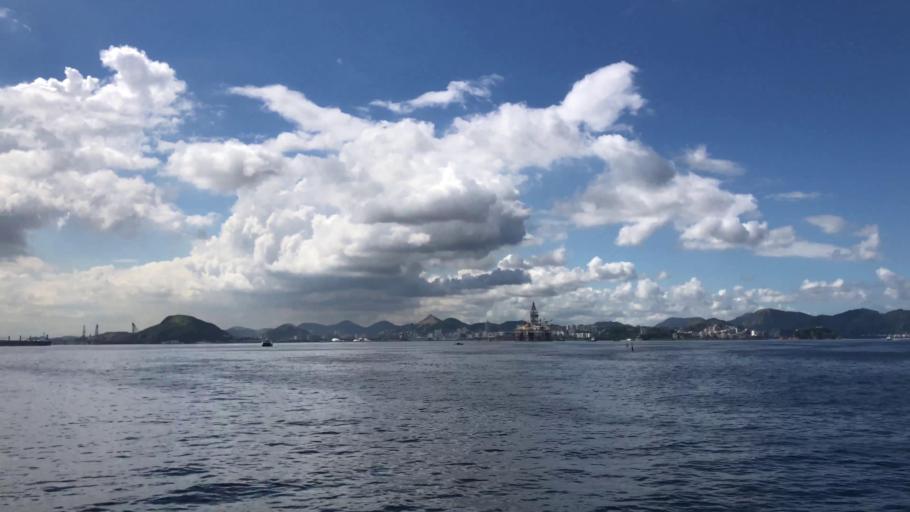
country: BR
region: Rio de Janeiro
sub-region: Rio De Janeiro
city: Rio de Janeiro
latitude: -22.9005
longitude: -43.1626
